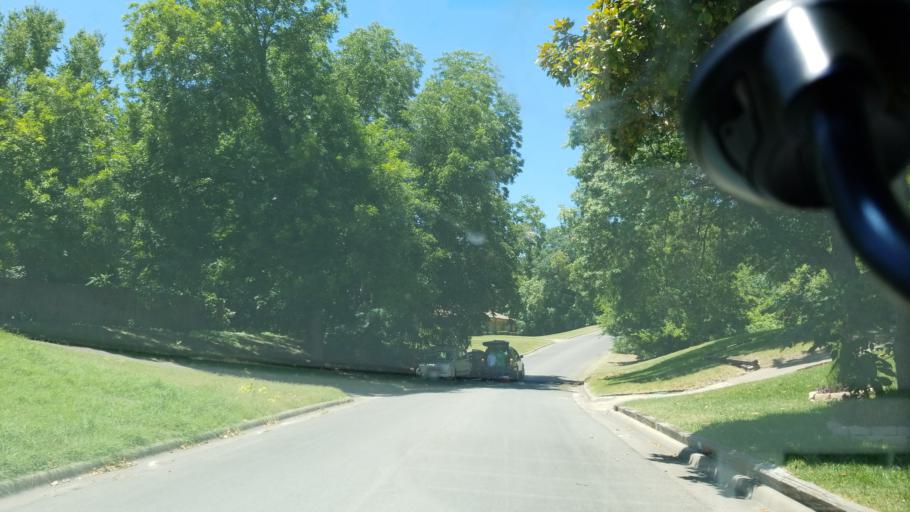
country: US
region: Texas
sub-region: Dallas County
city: Cockrell Hill
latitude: 32.6921
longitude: -96.8375
